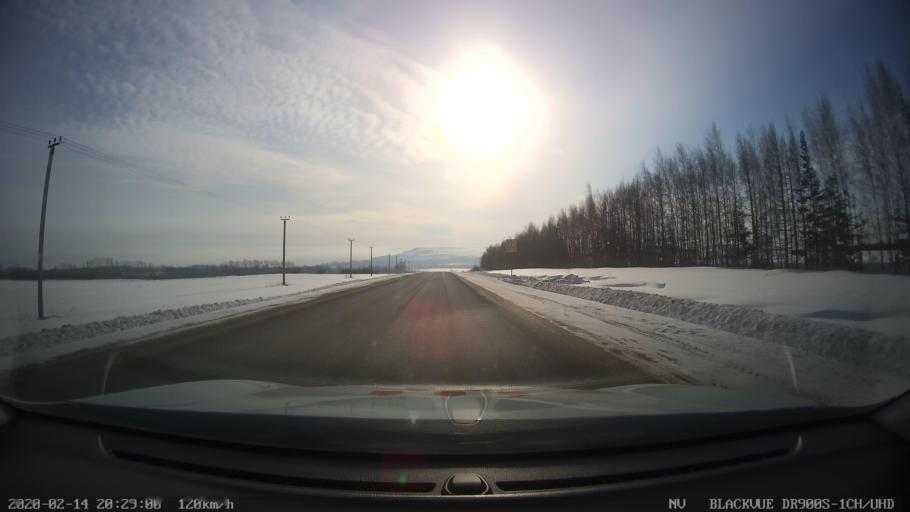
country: RU
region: Tatarstan
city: Stolbishchi
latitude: 55.4547
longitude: 48.9790
